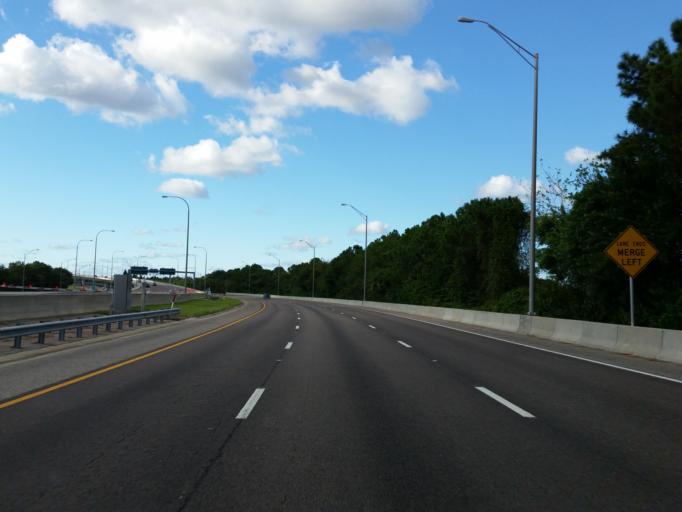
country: US
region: Florida
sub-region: Hillsborough County
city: Palm River-Clair Mel
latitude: 27.9450
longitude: -82.3617
